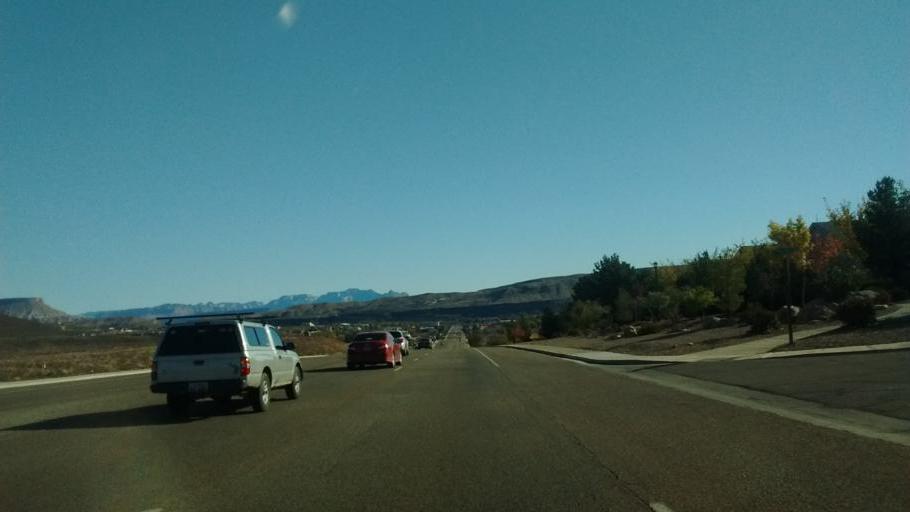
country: US
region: Utah
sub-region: Washington County
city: Hurricane
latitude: 37.1763
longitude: -113.3257
